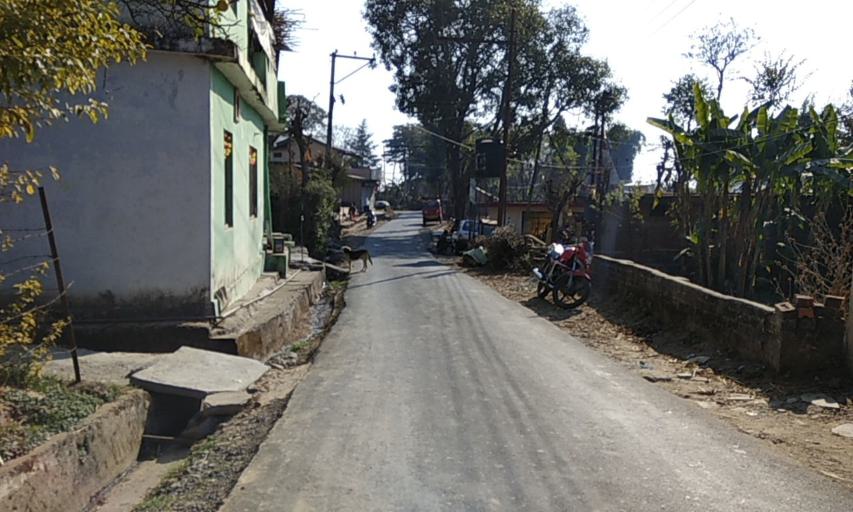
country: IN
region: Himachal Pradesh
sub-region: Kangra
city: Palampur
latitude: 32.1167
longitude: 76.5252
